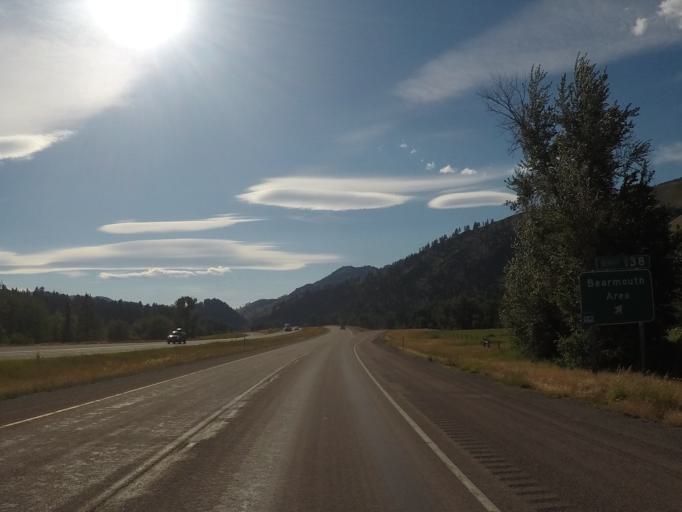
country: US
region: Montana
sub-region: Missoula County
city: Clinton
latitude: 46.6976
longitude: -113.4257
